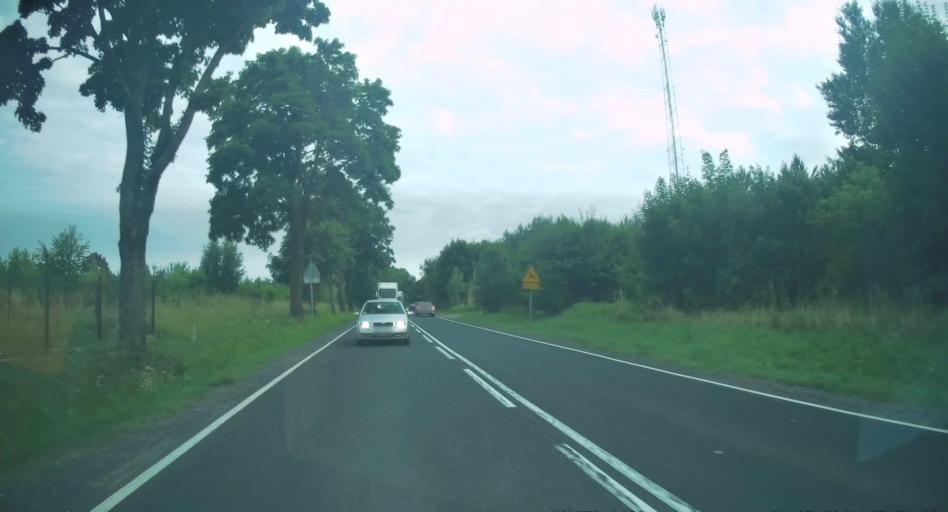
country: PL
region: Lodz Voivodeship
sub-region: Powiat radomszczanski
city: Gomunice
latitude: 51.1518
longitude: 19.4897
